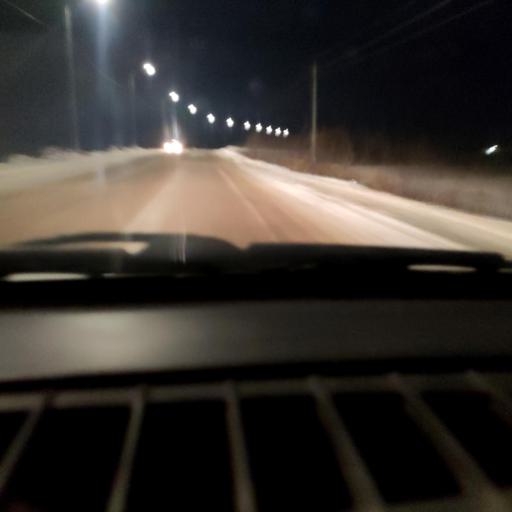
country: RU
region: Bashkortostan
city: Ulukulevo
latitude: 54.5661
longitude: 56.3373
